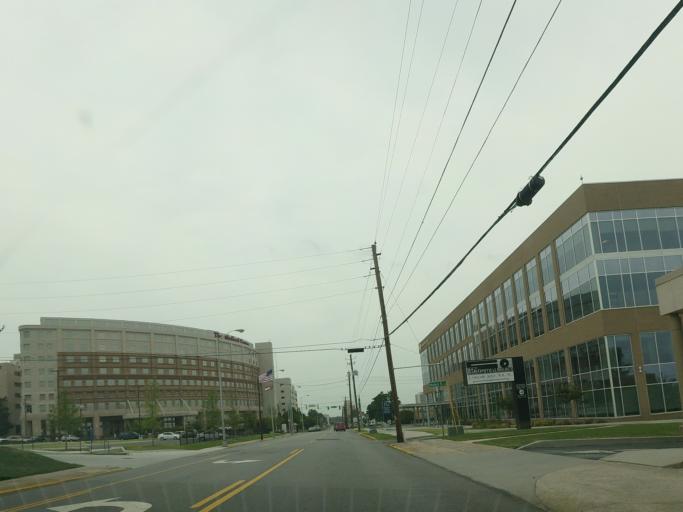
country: US
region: Georgia
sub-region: Bibb County
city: Macon
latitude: 32.8315
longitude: -83.6356
